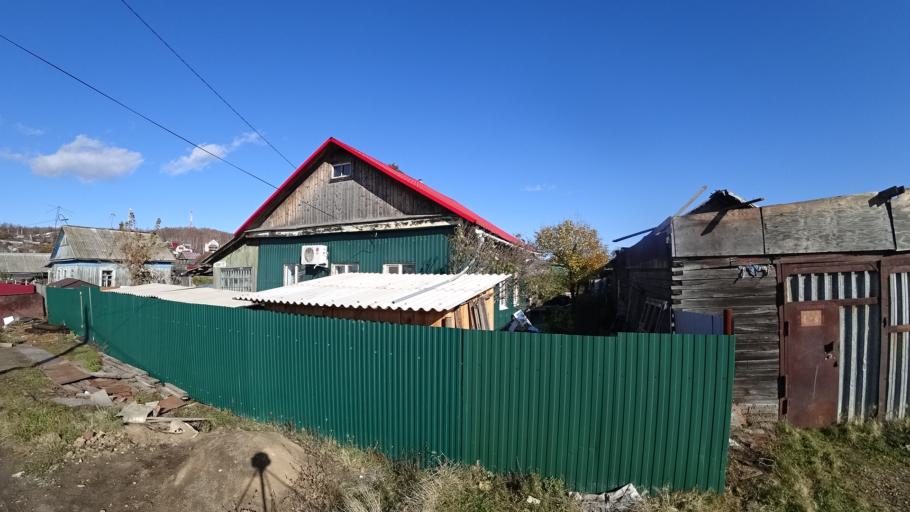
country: RU
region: Khabarovsk Krai
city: Amursk
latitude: 50.2347
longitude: 136.9212
